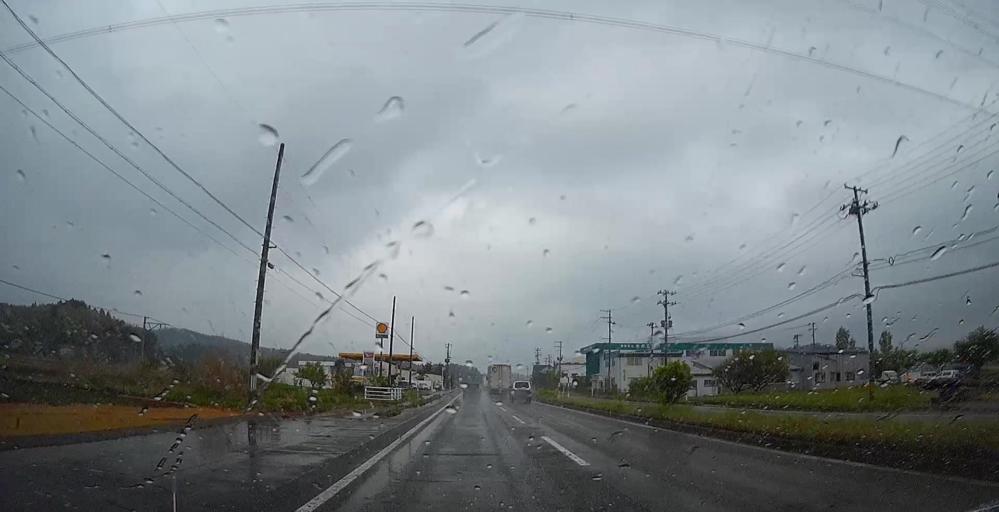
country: JP
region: Niigata
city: Kashiwazaki
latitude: 37.4421
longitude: 138.6318
